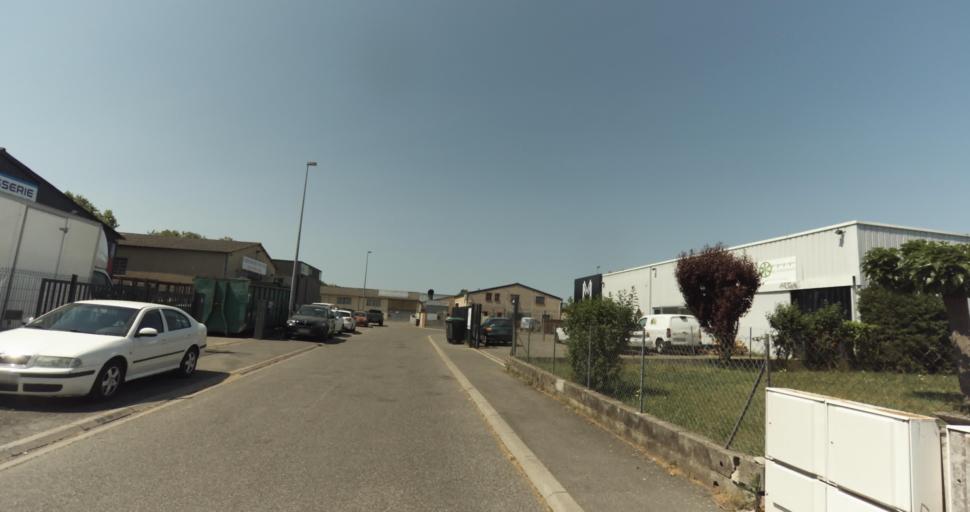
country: FR
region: Midi-Pyrenees
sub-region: Departement de la Haute-Garonne
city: Plaisance-du-Touch
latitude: 43.5627
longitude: 1.2880
